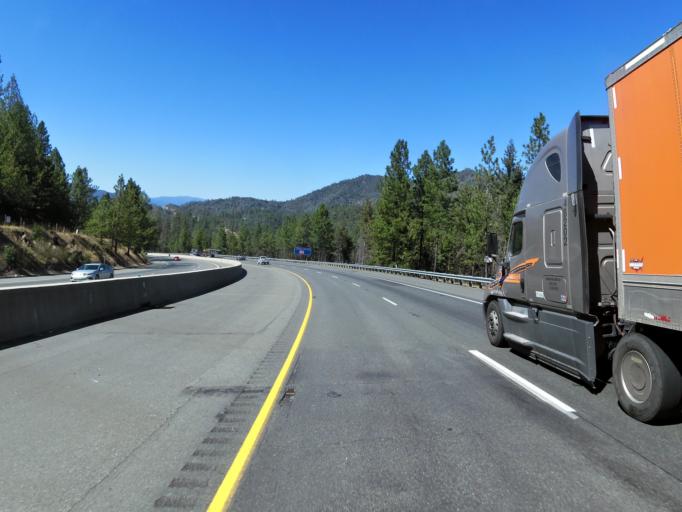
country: US
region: California
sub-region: Shasta County
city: Shasta Lake
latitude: 40.8426
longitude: -122.3282
